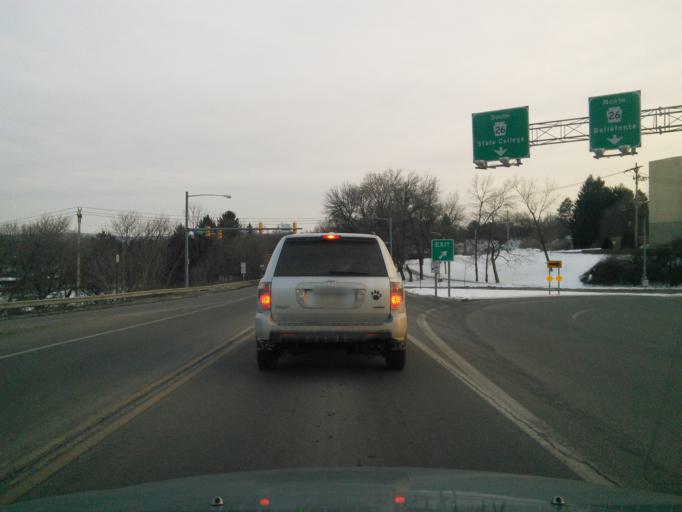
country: US
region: Pennsylvania
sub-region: Centre County
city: State College
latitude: 40.8018
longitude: -77.8505
